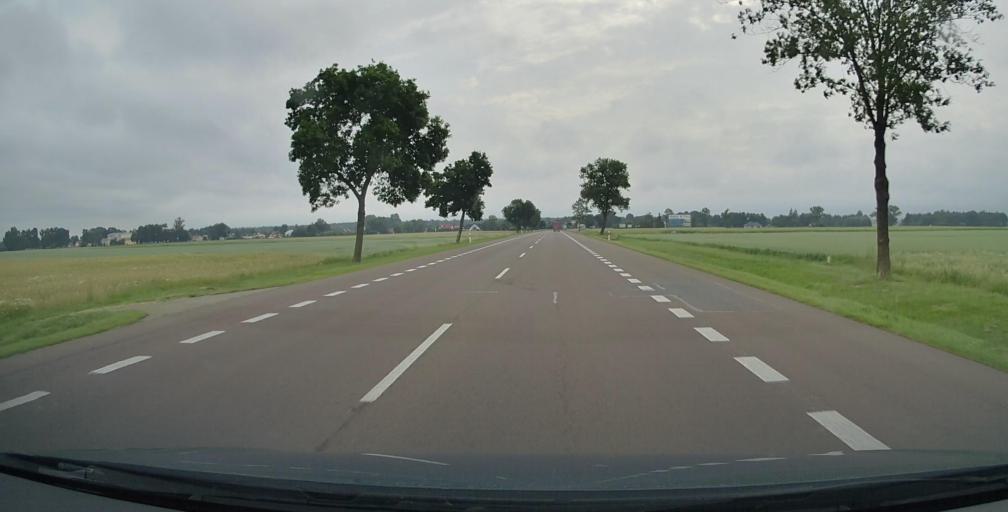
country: PL
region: Lublin Voivodeship
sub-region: Powiat bialski
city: Miedzyrzec Podlaski
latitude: 52.0246
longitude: 22.8609
